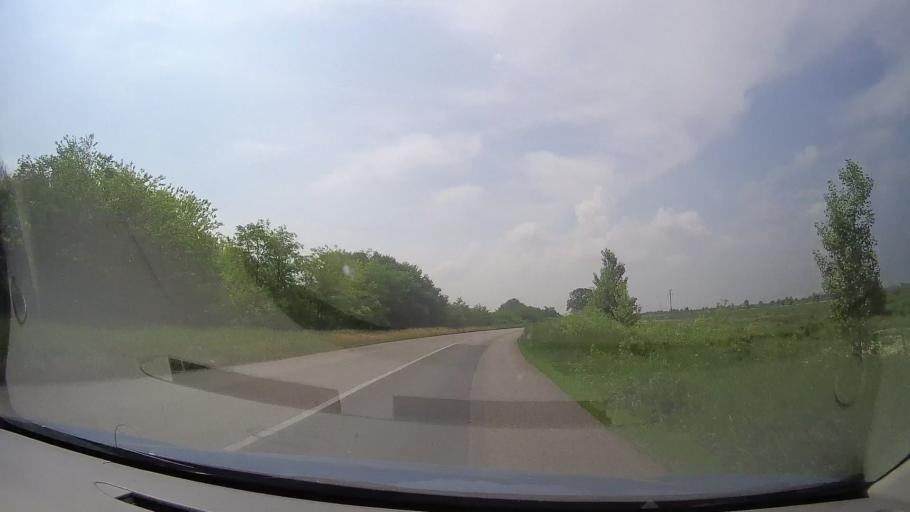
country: RS
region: Autonomna Pokrajina Vojvodina
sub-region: Juznobanatski Okrug
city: Kovacica
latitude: 45.0816
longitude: 20.6411
